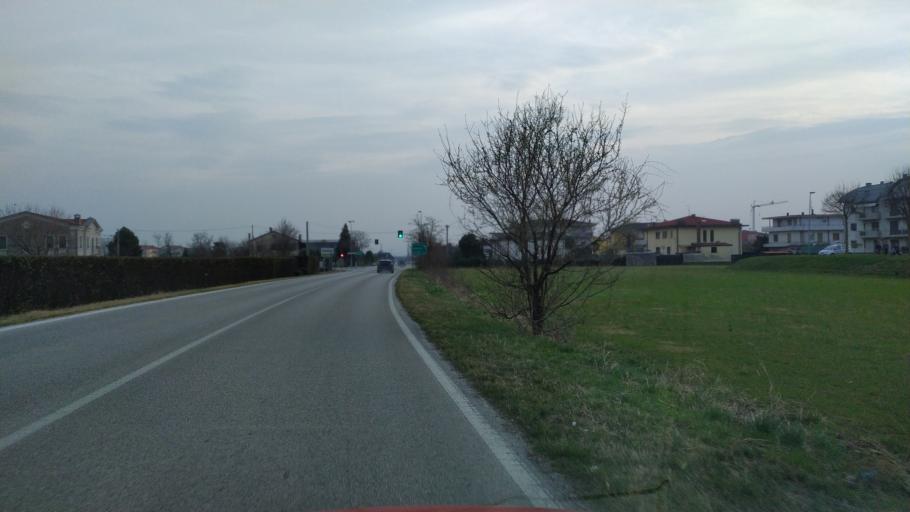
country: IT
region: Veneto
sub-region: Provincia di Vicenza
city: Dueville
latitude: 45.6428
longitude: 11.5576
